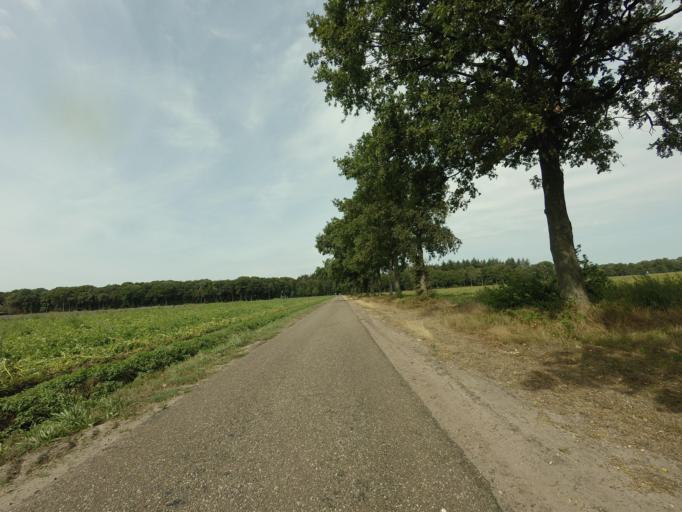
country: NL
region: North Brabant
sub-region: Gemeente Sint Anthonis
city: Sint Anthonis
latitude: 51.5568
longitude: 5.8169
